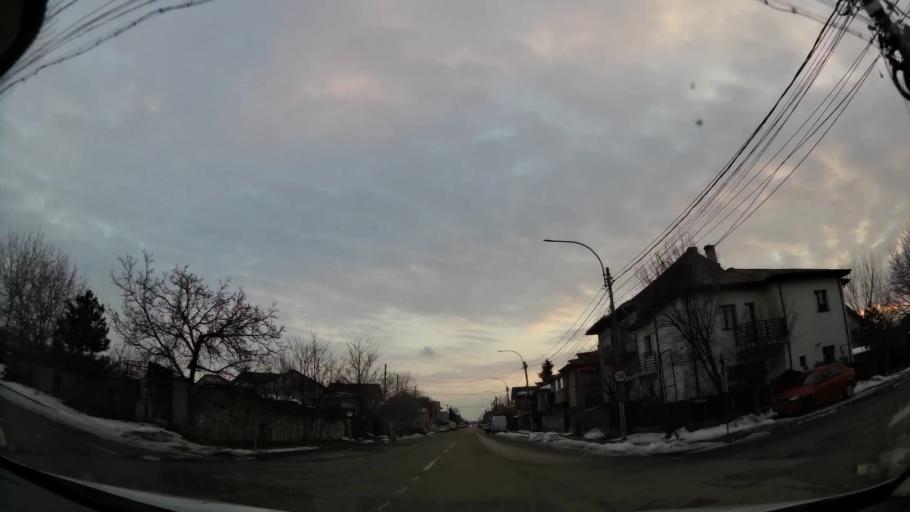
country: RO
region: Ilfov
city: Dobroesti
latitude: 44.4529
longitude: 26.1855
